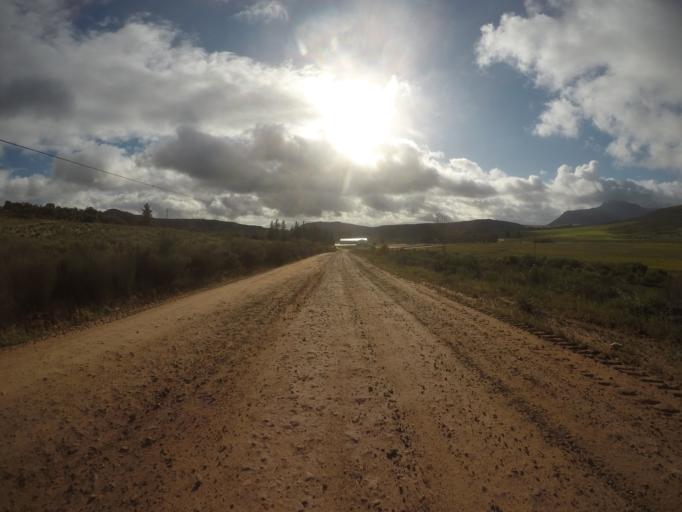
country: ZA
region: Western Cape
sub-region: West Coast District Municipality
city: Clanwilliam
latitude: -32.3427
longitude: 18.8294
